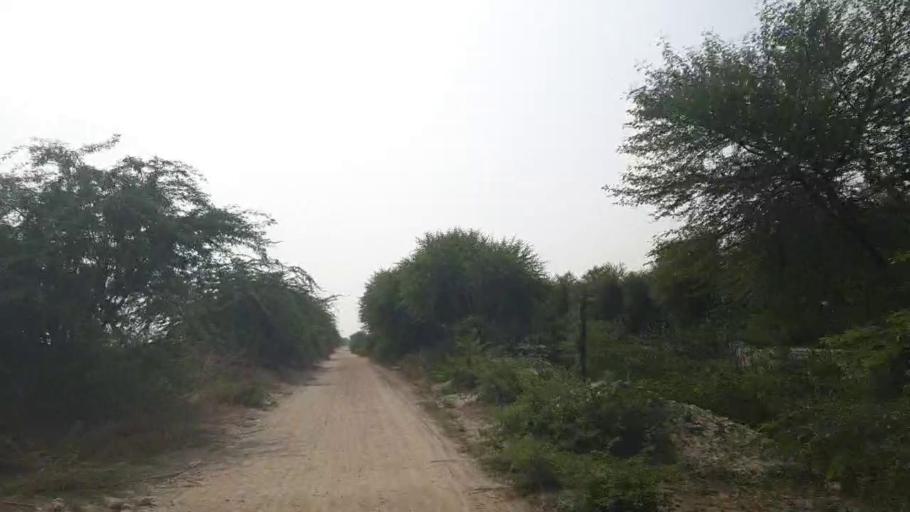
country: PK
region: Sindh
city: Badin
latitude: 24.6085
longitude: 68.7207
